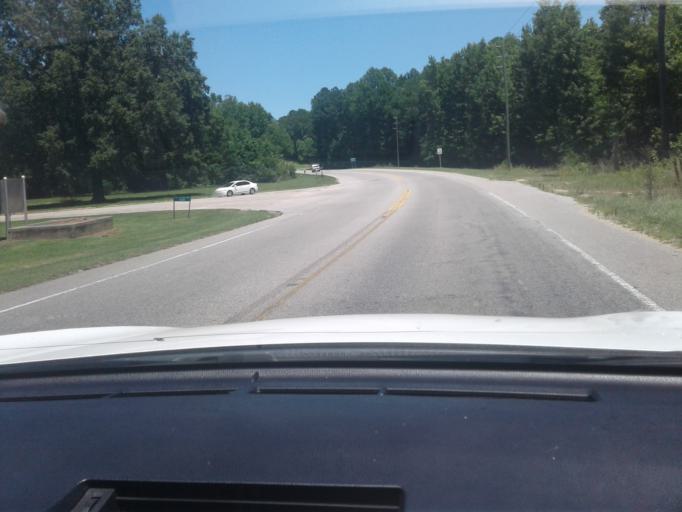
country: US
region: North Carolina
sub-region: Harnett County
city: Erwin
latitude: 35.3123
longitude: -78.6911
